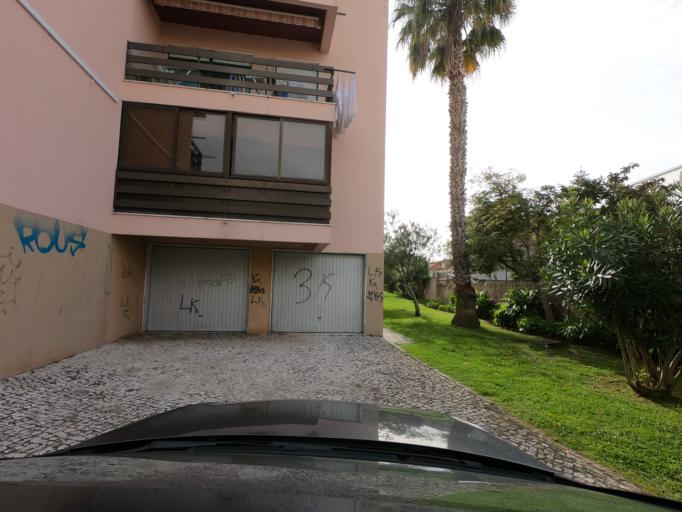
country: PT
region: Lisbon
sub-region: Oeiras
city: Carcavelos
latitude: 38.6944
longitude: -9.3244
